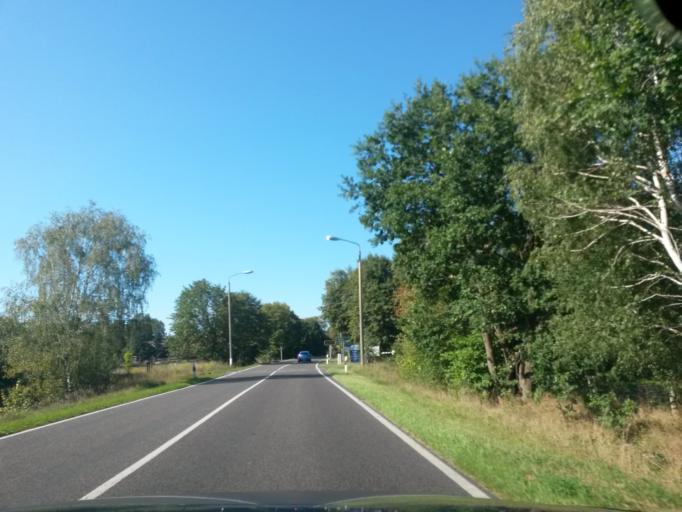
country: DE
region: Brandenburg
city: Templin
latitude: 53.1406
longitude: 13.4231
